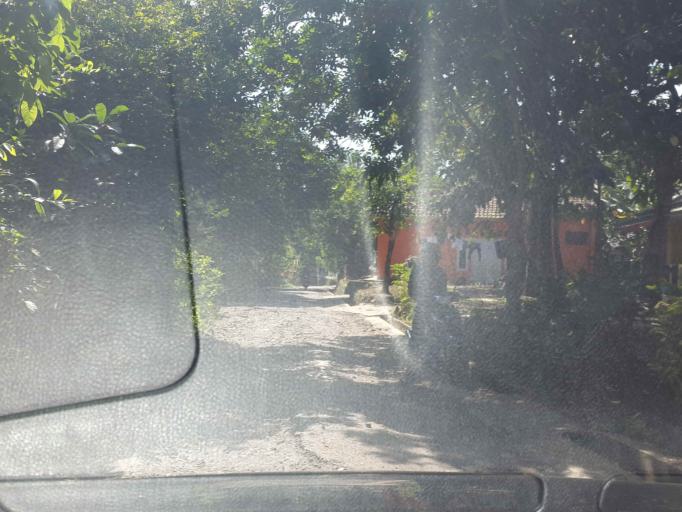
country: ID
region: West Java
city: Ciranjang-hilir
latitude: -6.7881
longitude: 107.2016
